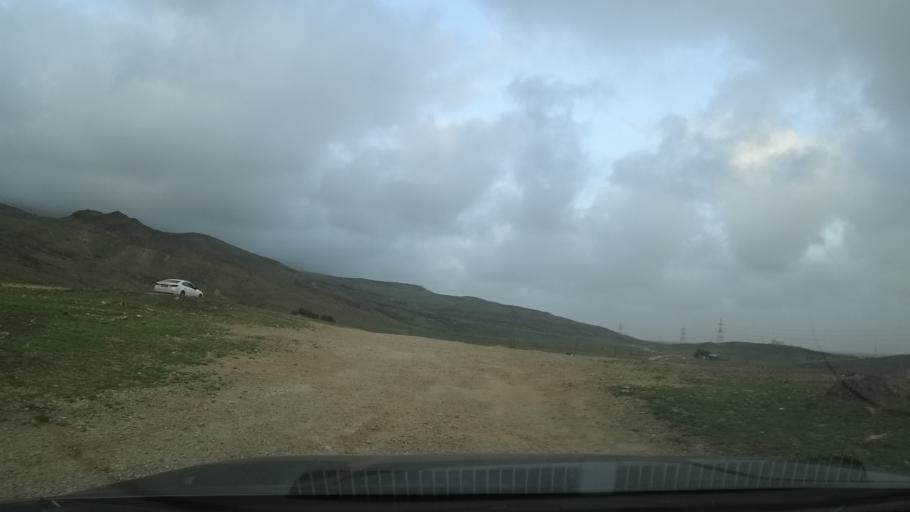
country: OM
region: Zufar
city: Salalah
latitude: 17.1180
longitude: 54.2300
